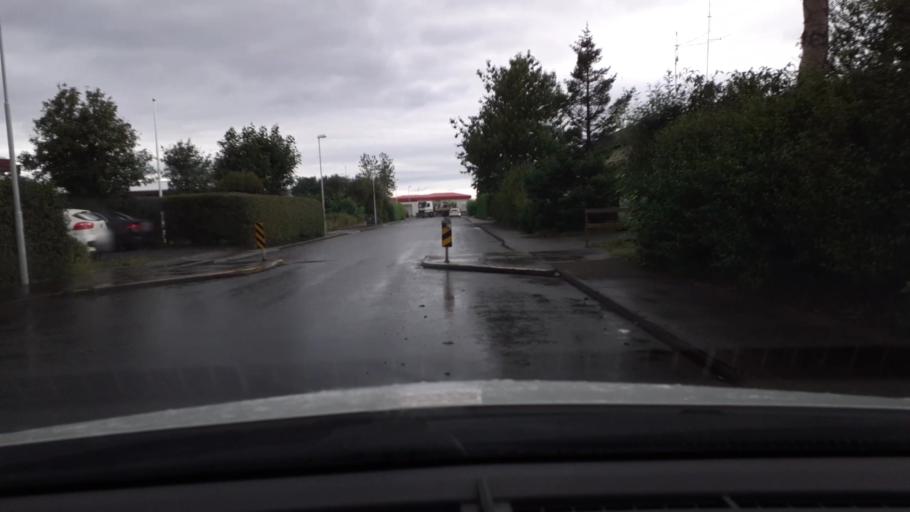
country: IS
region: West
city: Akranes
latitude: 64.3161
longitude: -22.0443
